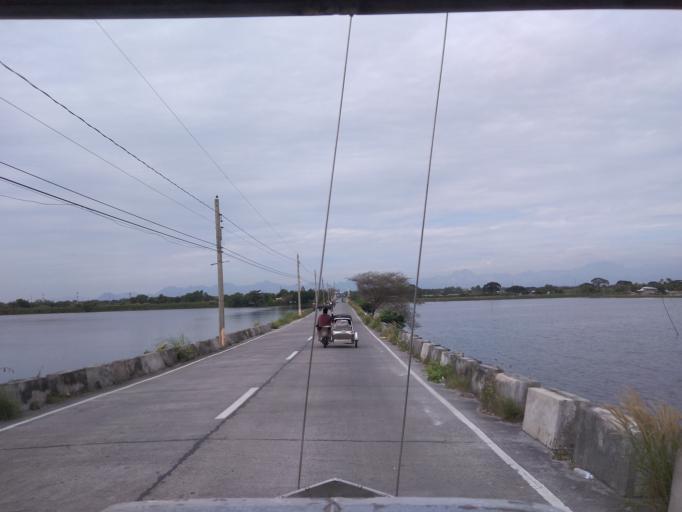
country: PH
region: Central Luzon
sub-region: Province of Pampanga
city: Lubao
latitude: 14.9377
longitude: 120.6125
